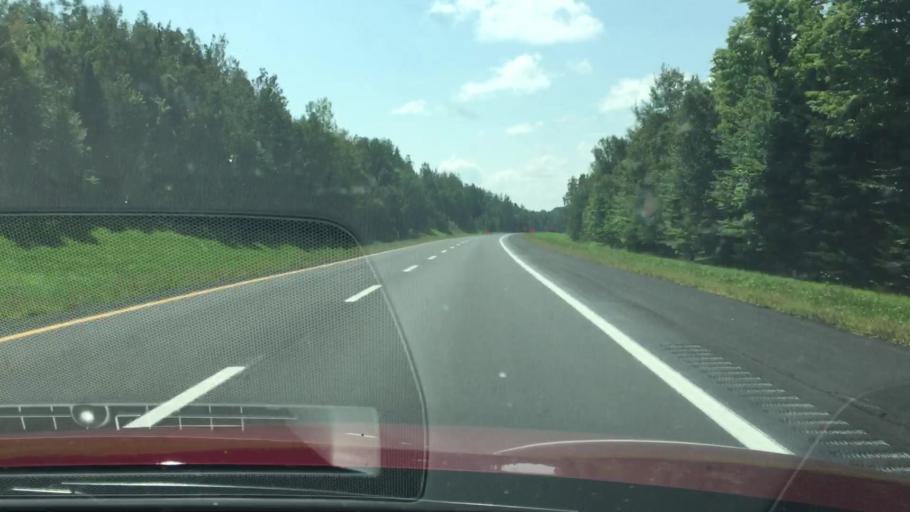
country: US
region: Maine
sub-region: Penobscot County
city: Patten
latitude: 45.9063
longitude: -68.3840
